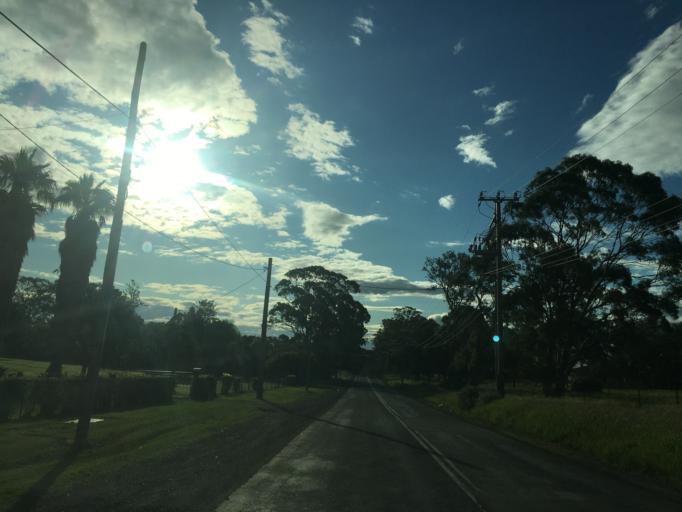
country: AU
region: New South Wales
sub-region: Campbelltown Municipality
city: Denham Court
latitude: -33.9739
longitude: 150.8066
